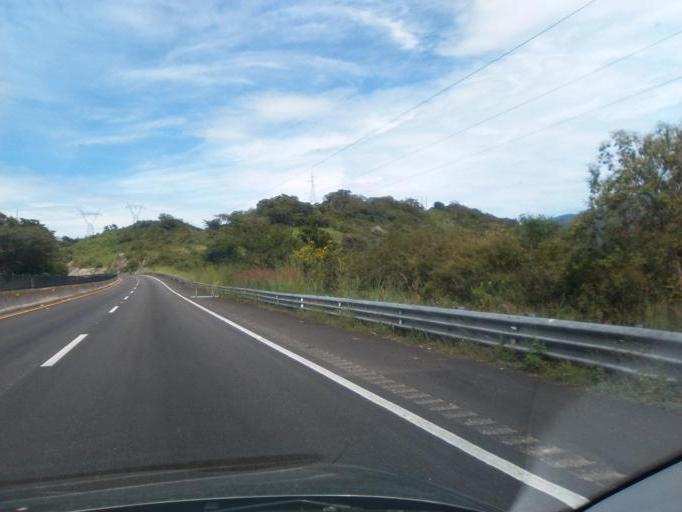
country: MX
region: Guerrero
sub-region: Chilpancingo de los Bravo
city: Acahuizotla
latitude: 17.3466
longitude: -99.4789
